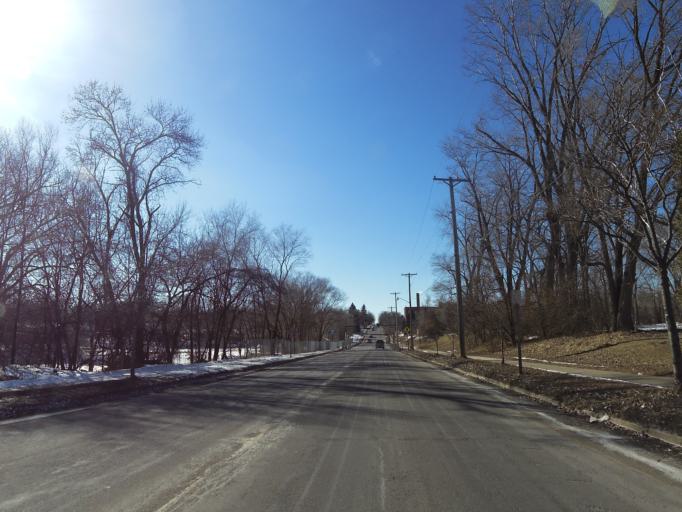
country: US
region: Minnesota
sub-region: Ramsey County
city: Saint Paul
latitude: 44.9568
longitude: -93.0507
